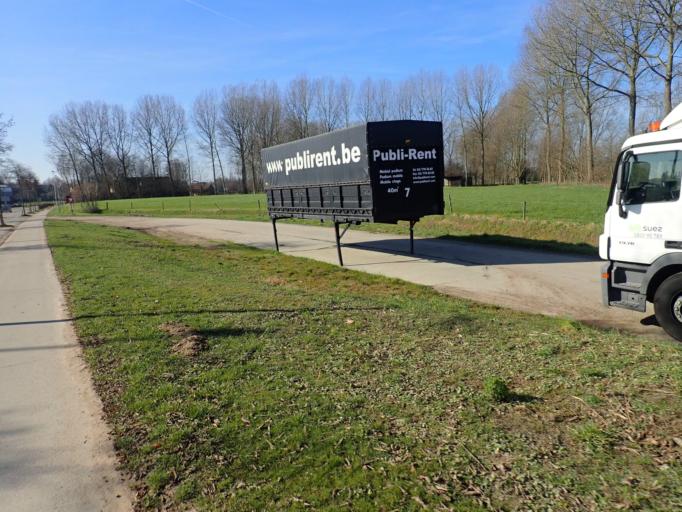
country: BE
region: Flanders
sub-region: Provincie Oost-Vlaanderen
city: Kruibeke
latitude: 51.1357
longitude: 4.2826
